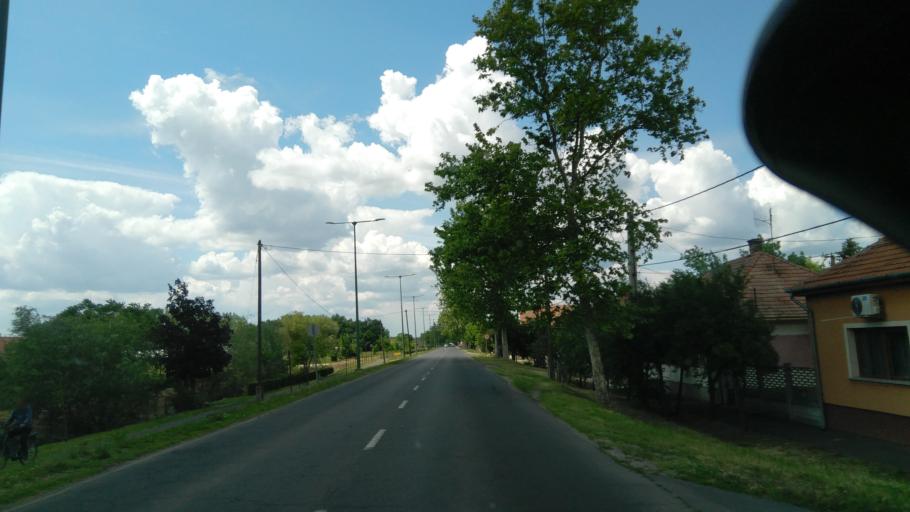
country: HU
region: Bekes
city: Gyula
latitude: 46.6485
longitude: 21.2505
